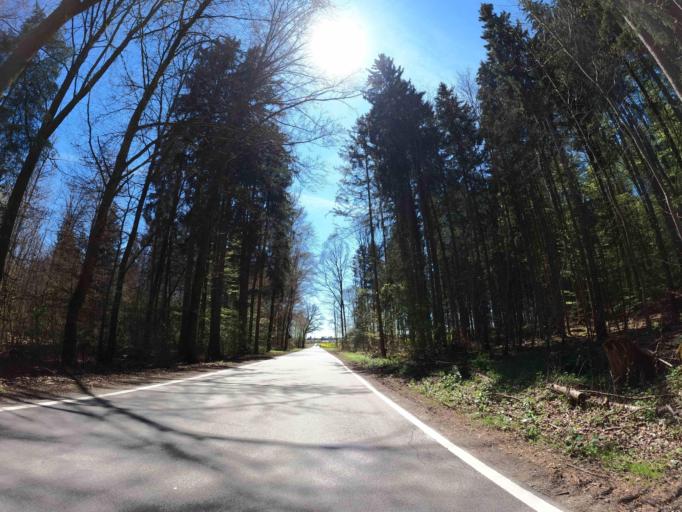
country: DE
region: Bavaria
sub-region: Upper Bavaria
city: Oberhaching
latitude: 48.0016
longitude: 11.5609
